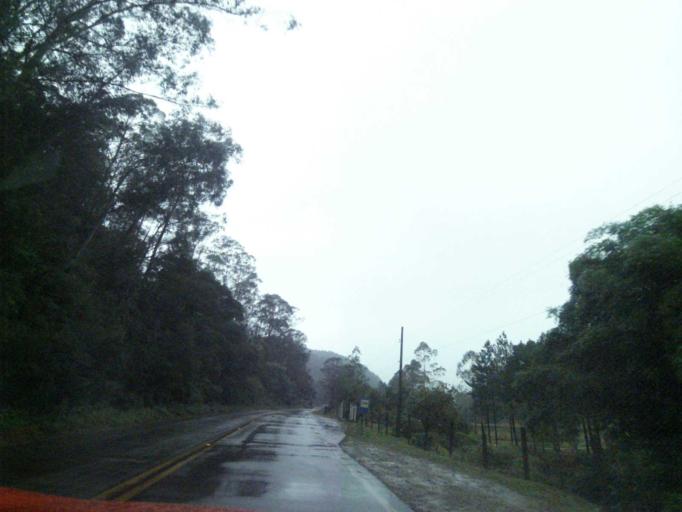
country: BR
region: Santa Catarina
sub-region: Anitapolis
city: Anitapolis
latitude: -27.8098
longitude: -49.0470
